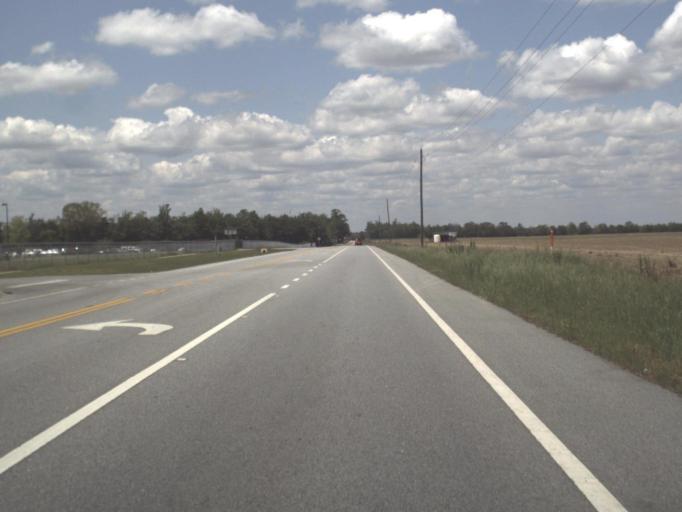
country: US
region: Florida
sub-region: Escambia County
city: Molino
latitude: 30.7405
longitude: -87.3603
